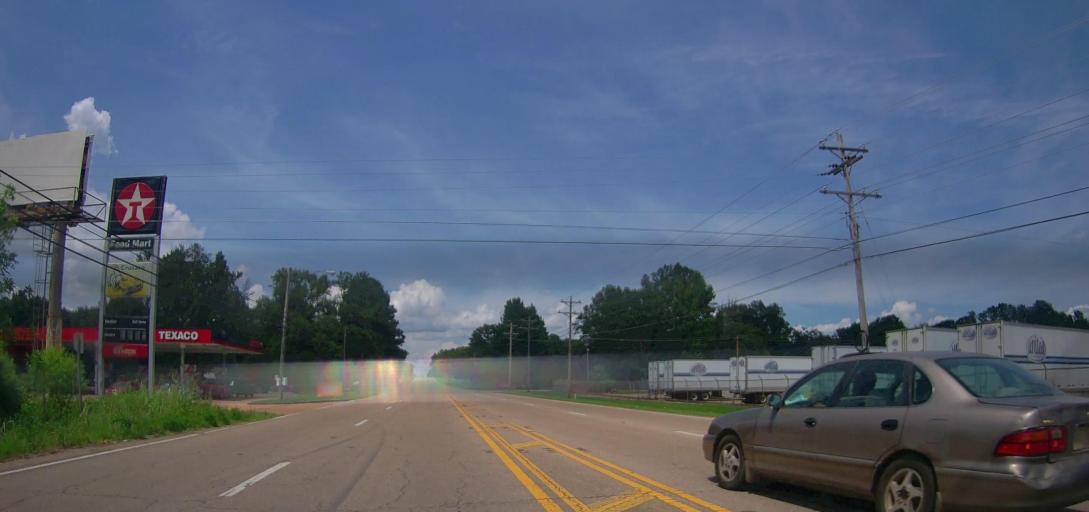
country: US
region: Mississippi
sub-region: Lee County
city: Verona
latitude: 34.1689
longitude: -88.7196
